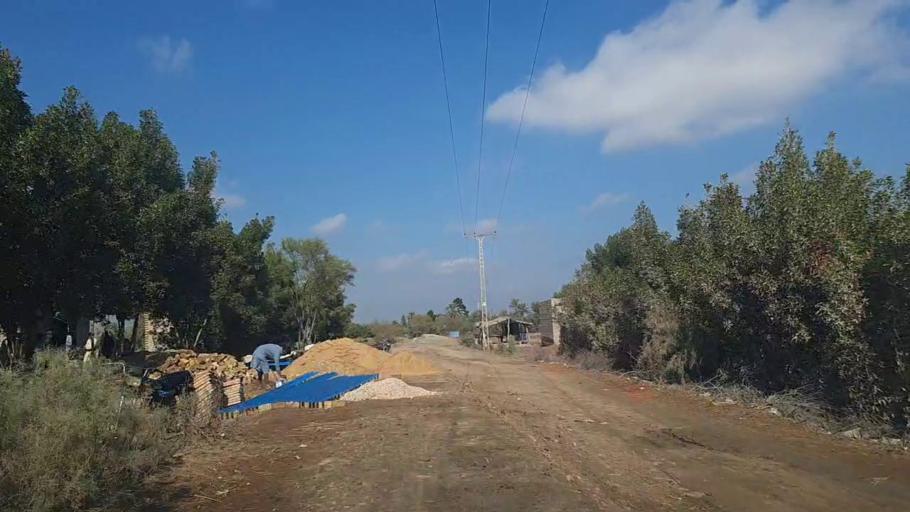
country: PK
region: Sindh
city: Sanghar
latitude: 26.0799
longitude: 68.9866
